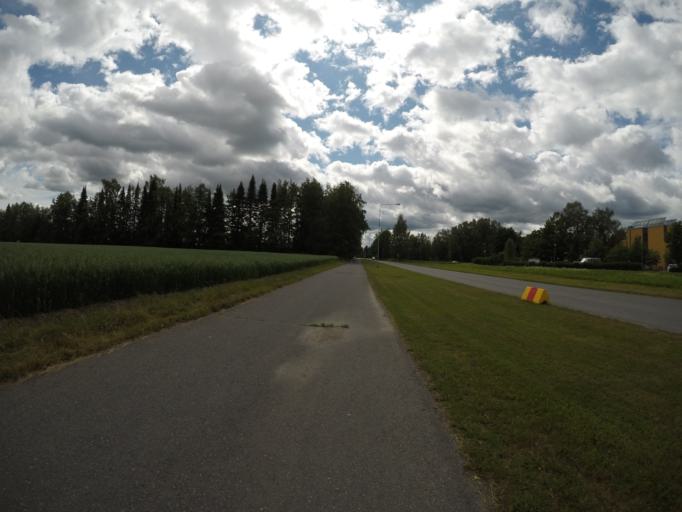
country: FI
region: Haeme
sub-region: Haemeenlinna
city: Haemeenlinna
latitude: 60.9786
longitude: 24.4262
